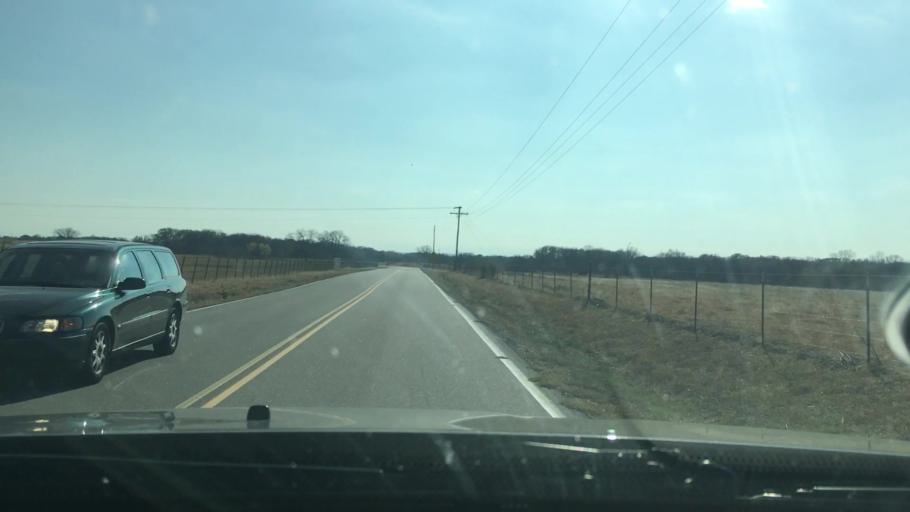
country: US
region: Oklahoma
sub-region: Marshall County
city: Oakland
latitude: 34.0285
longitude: -96.9348
